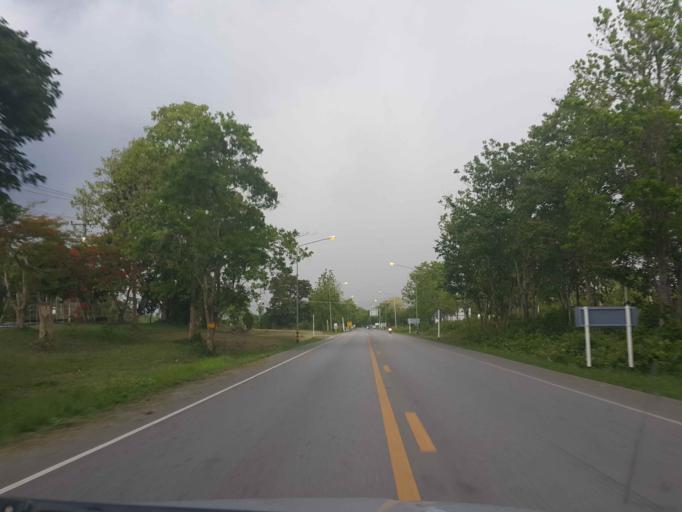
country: TH
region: Phrae
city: Den Chai
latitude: 17.9775
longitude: 100.0350
